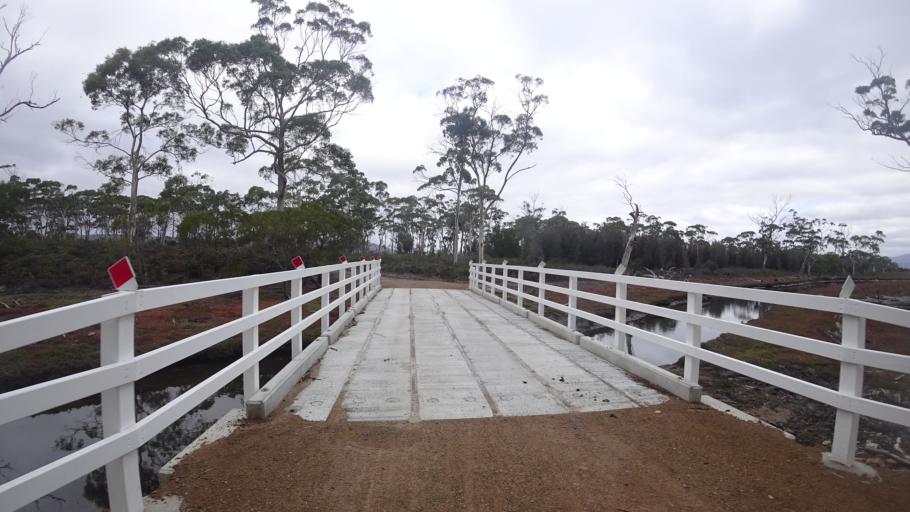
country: AU
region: Tasmania
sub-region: Sorell
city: Sorell
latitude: -42.6530
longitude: 148.0455
